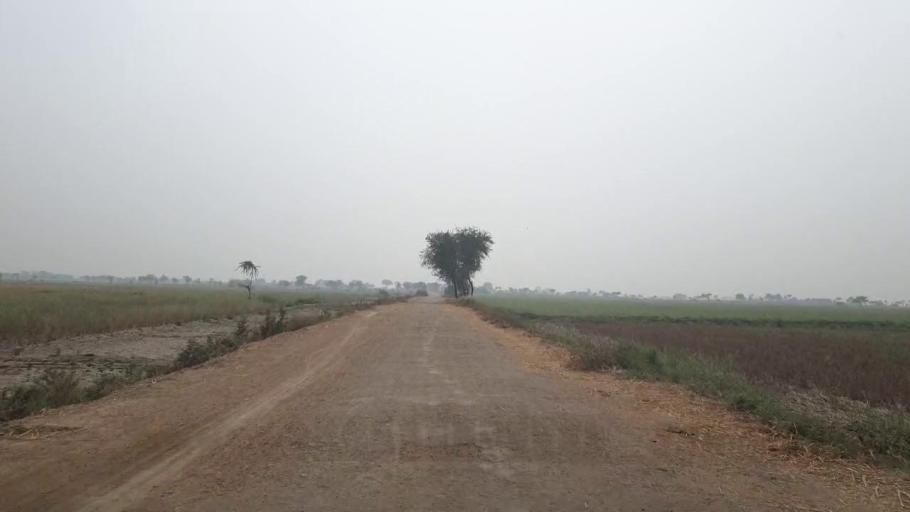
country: PK
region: Sindh
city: Kario
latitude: 24.6510
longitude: 68.6217
